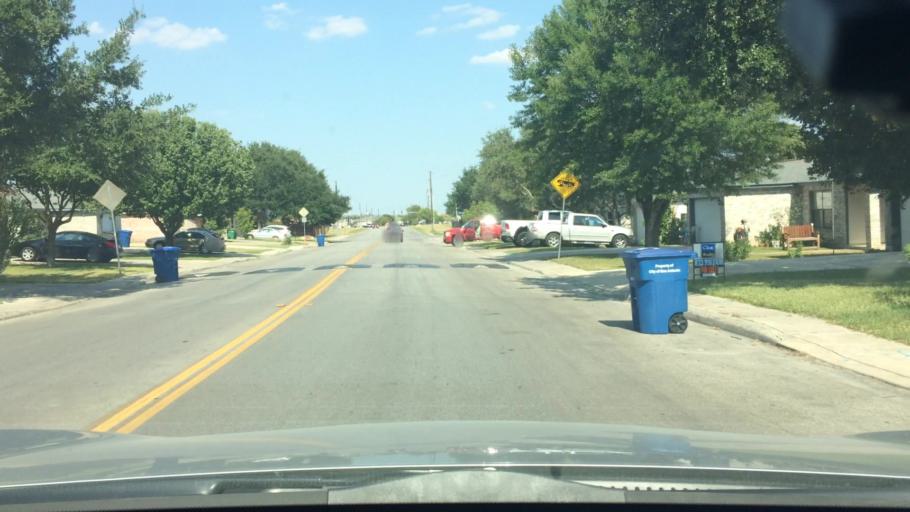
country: US
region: Texas
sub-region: Bexar County
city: Kirby
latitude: 29.4677
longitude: -98.3633
